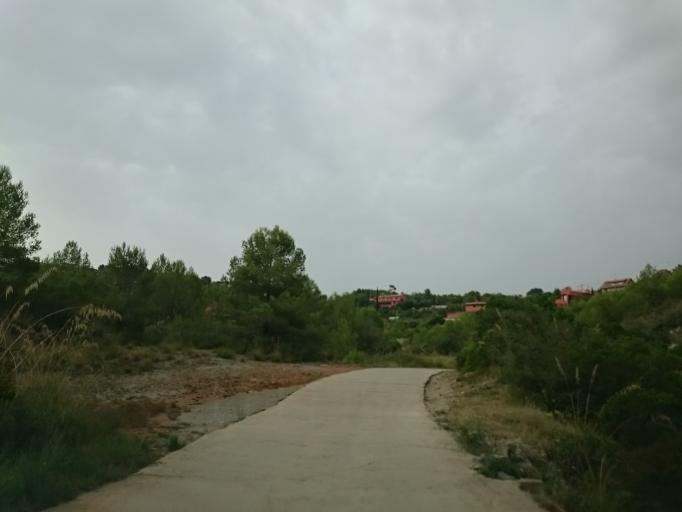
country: ES
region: Catalonia
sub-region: Provincia de Barcelona
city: Olivella
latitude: 41.2954
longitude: 1.8583
